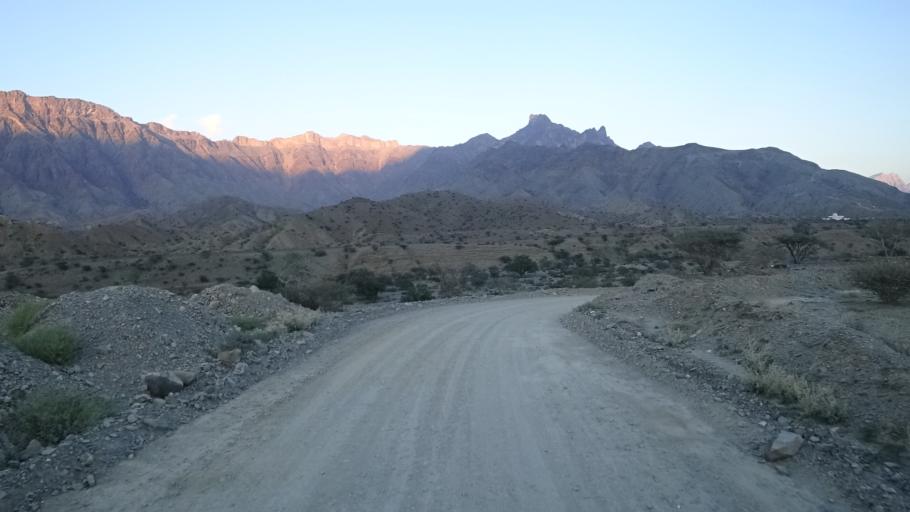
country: OM
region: Al Batinah
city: Rustaq
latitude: 23.2908
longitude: 57.3340
